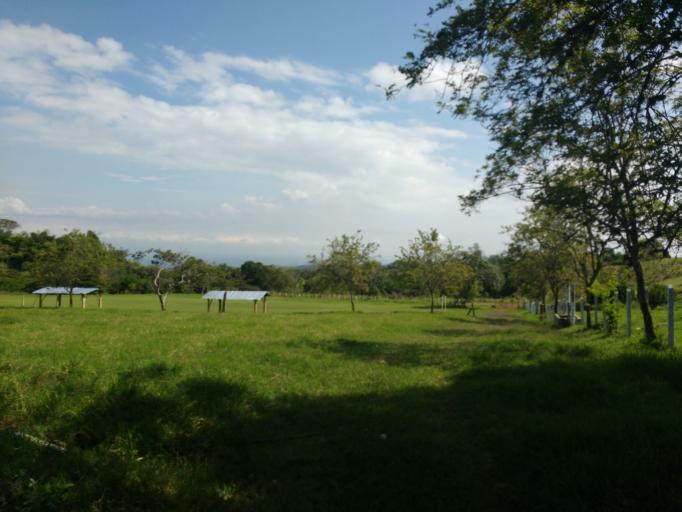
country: CO
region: Cauca
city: Santander de Quilichao
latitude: 2.9825
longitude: -76.4539
